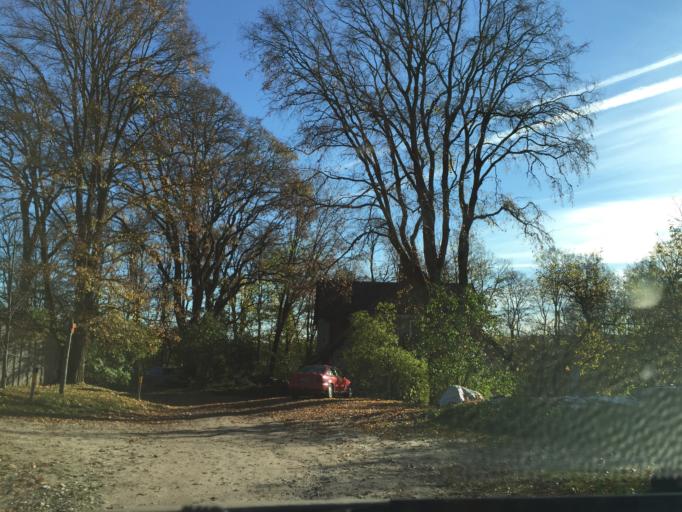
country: LV
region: Skriveri
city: Skriveri
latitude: 56.6153
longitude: 25.1581
